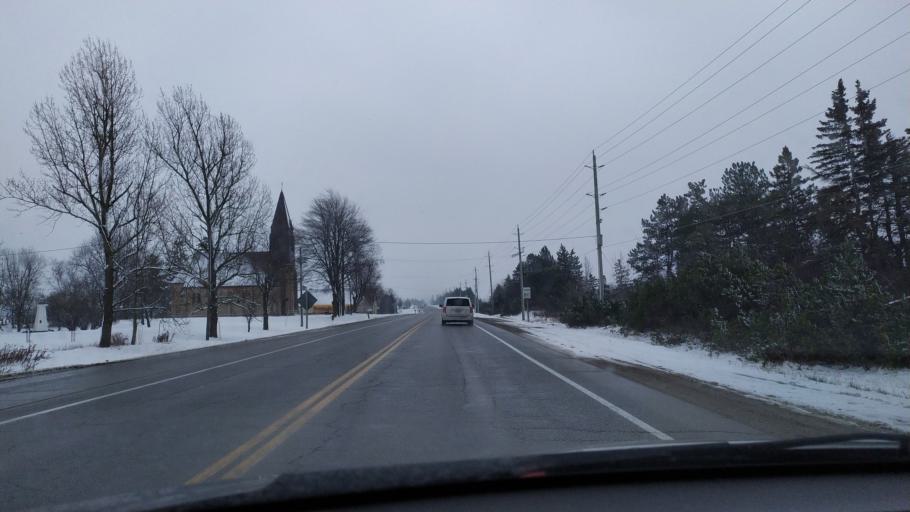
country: CA
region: Ontario
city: Waterloo
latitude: 43.6228
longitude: -80.6924
